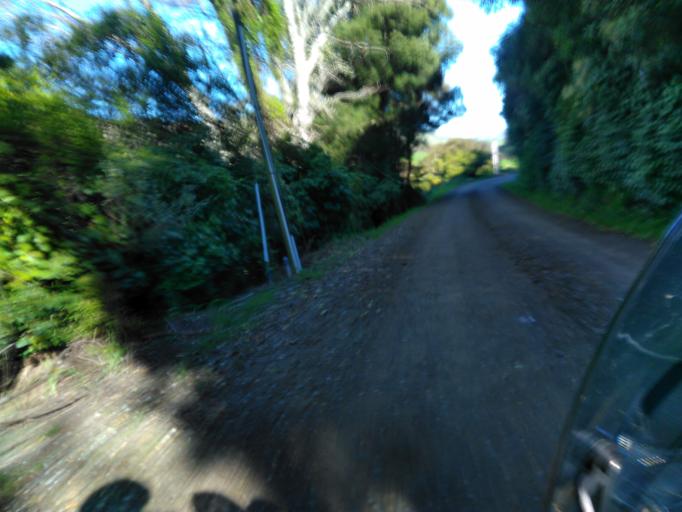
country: NZ
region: Gisborne
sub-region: Gisborne District
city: Gisborne
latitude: -38.4183
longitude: 177.6990
